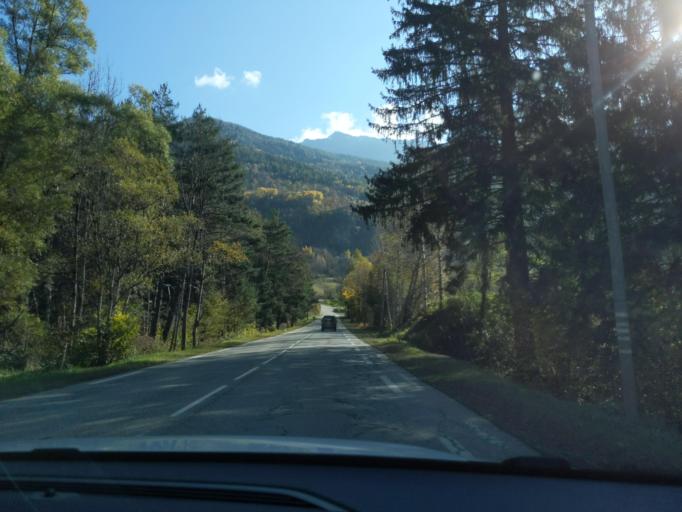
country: FR
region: Rhone-Alpes
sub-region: Departement de la Savoie
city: Seez
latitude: 45.5986
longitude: 6.8730
